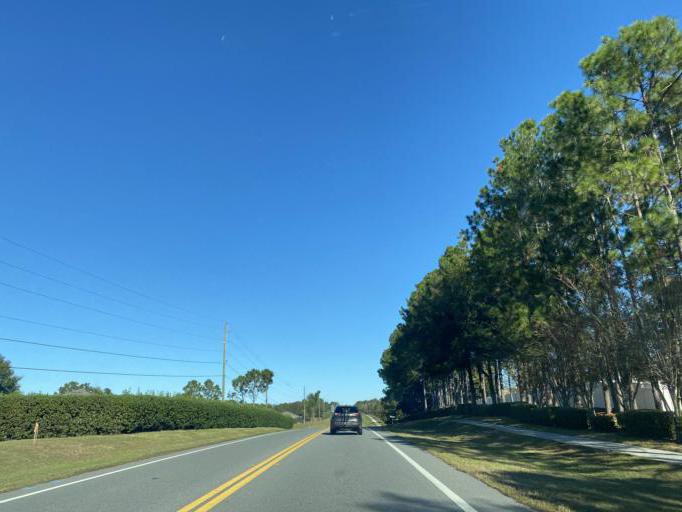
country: US
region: Florida
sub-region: Lake County
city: Clermont
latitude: 28.5016
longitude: -81.7071
